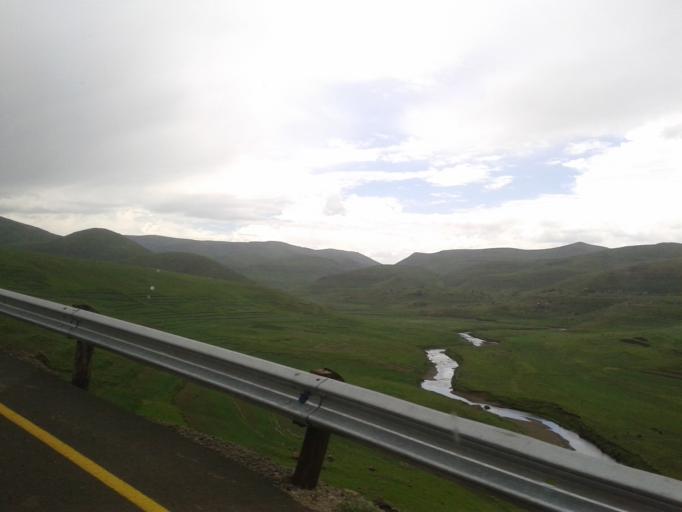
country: LS
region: Maseru
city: Nako
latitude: -29.7846
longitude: 28.0234
